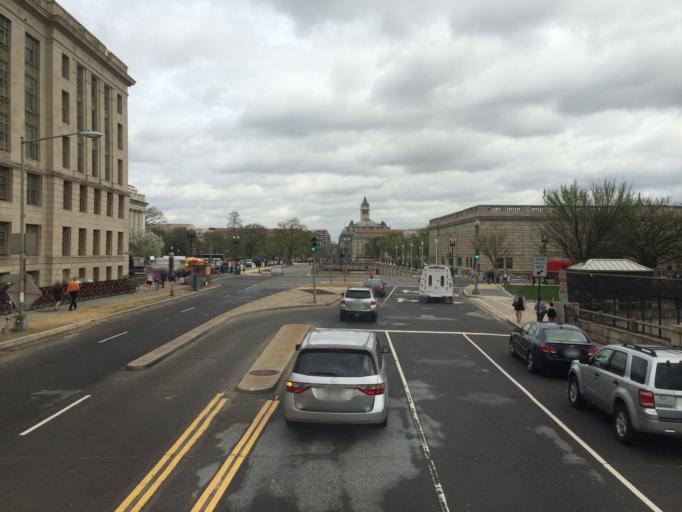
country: US
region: Washington, D.C.
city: Washington, D.C.
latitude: 38.8868
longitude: -77.0281
